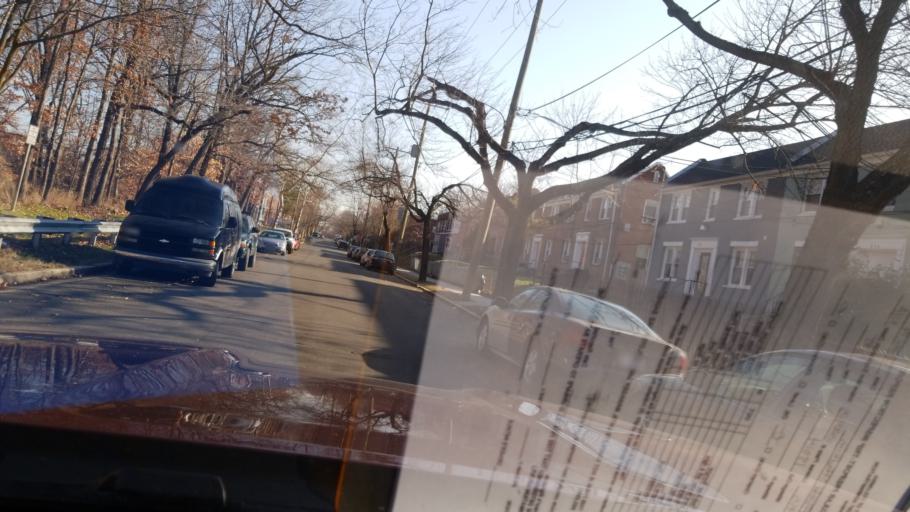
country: US
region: Maryland
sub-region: Prince George's County
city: Glassmanor
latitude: 38.8488
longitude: -77.0041
